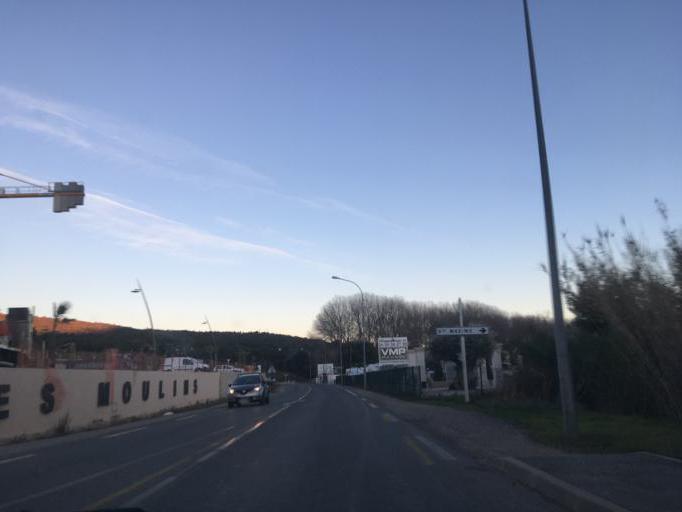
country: FR
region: Provence-Alpes-Cote d'Azur
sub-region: Departement du Var
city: Sainte-Maxime
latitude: 43.3276
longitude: 6.6114
